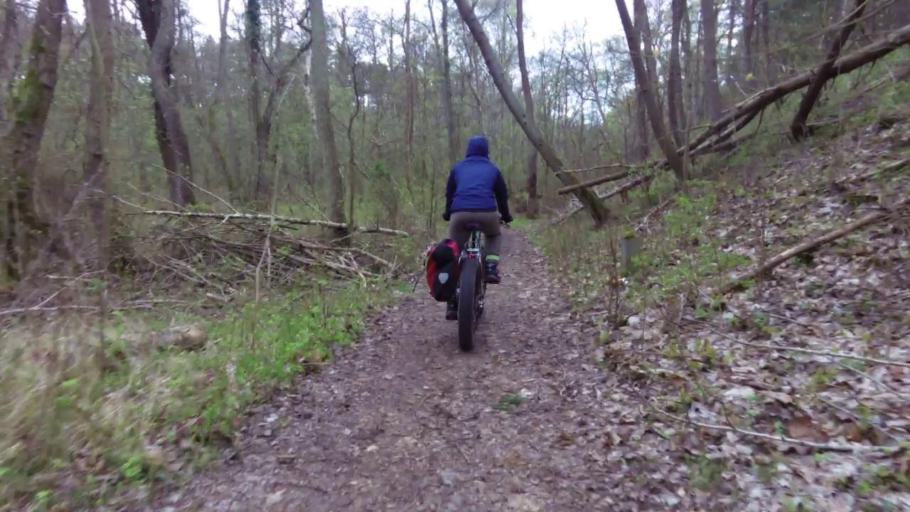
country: PL
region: West Pomeranian Voivodeship
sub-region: Powiat kamienski
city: Dziwnow
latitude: 54.0131
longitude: 14.7042
